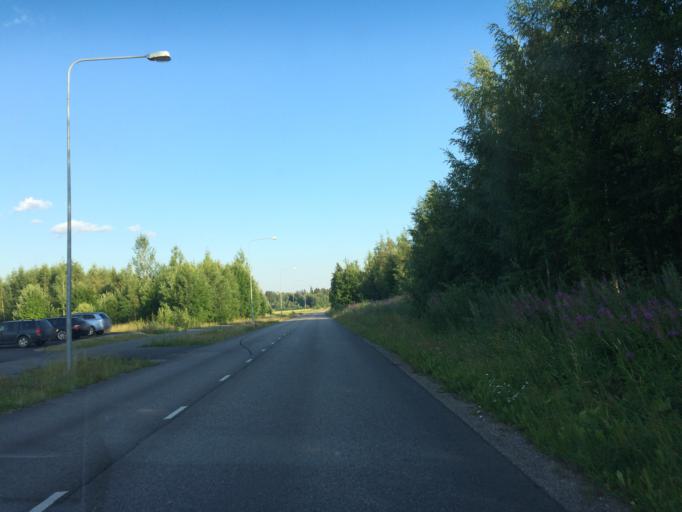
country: FI
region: Haeme
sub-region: Haemeenlinna
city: Parola
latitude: 61.0432
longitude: 24.3785
